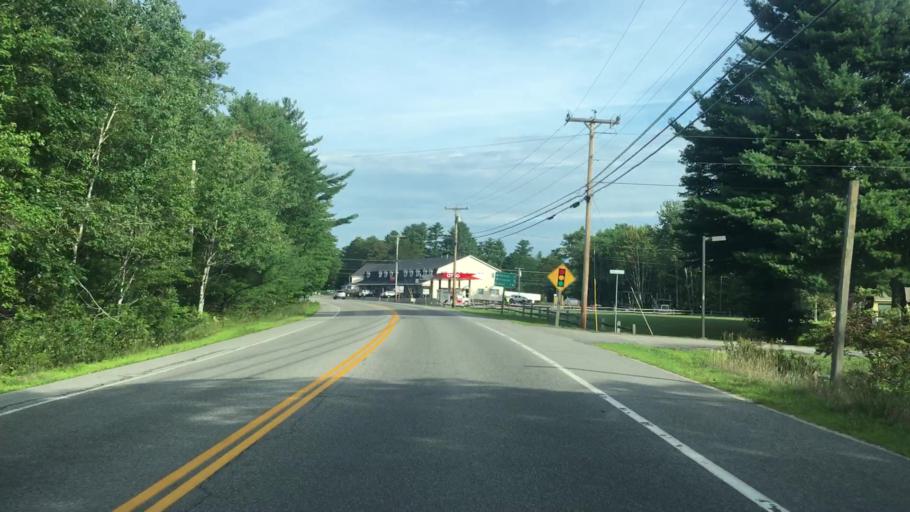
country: US
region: Maine
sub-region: York County
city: Limington
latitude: 43.7454
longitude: -70.6770
